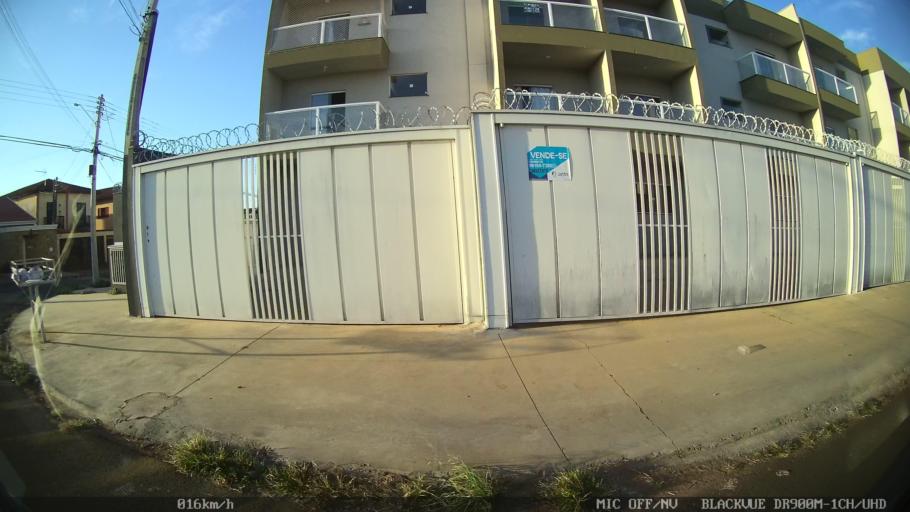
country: BR
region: Sao Paulo
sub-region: Franca
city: Franca
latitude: -20.5057
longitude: -47.3904
